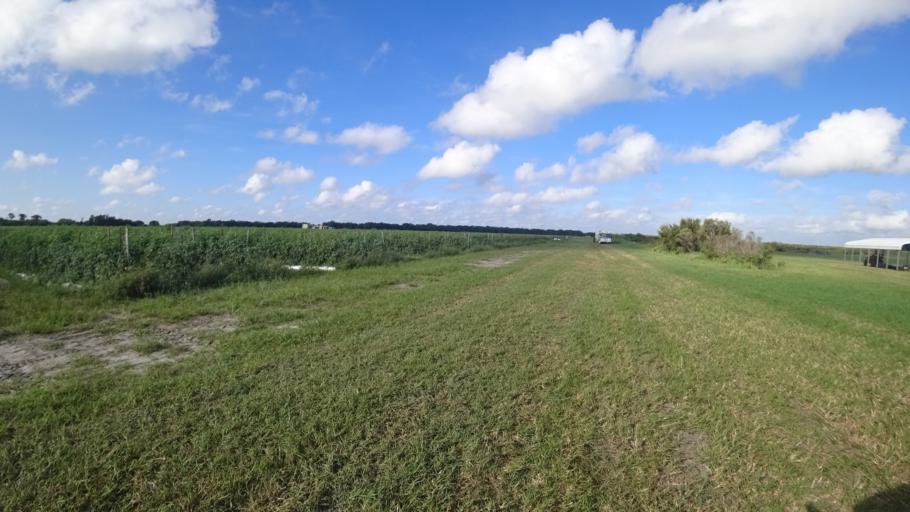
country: US
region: Florida
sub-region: Hillsborough County
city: Wimauma
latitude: 27.5567
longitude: -82.3250
